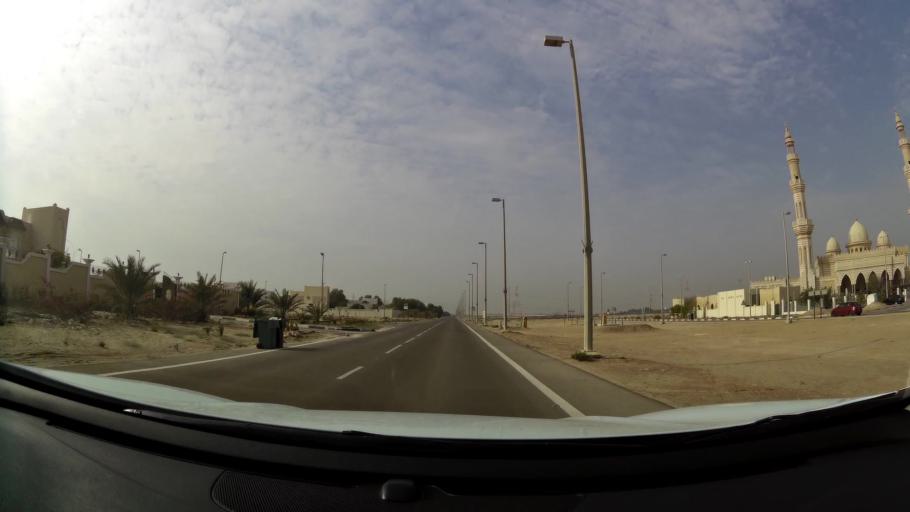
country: AE
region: Abu Dhabi
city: Abu Dhabi
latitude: 24.6647
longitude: 54.7612
